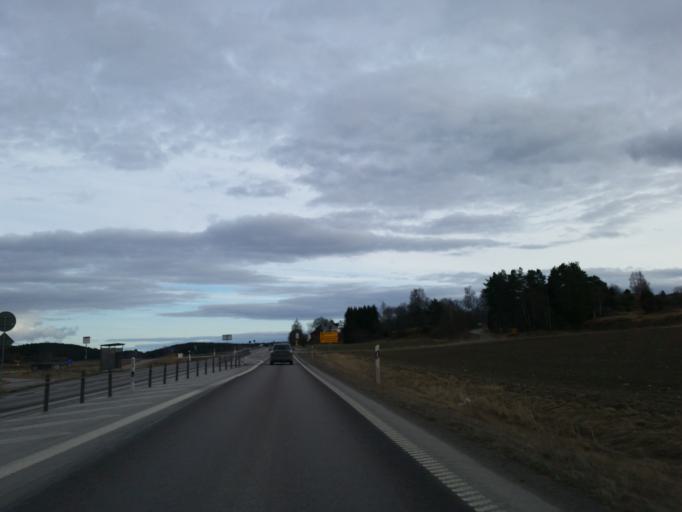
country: SE
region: OEstergoetland
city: Lindo
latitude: 58.5434
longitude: 16.2695
